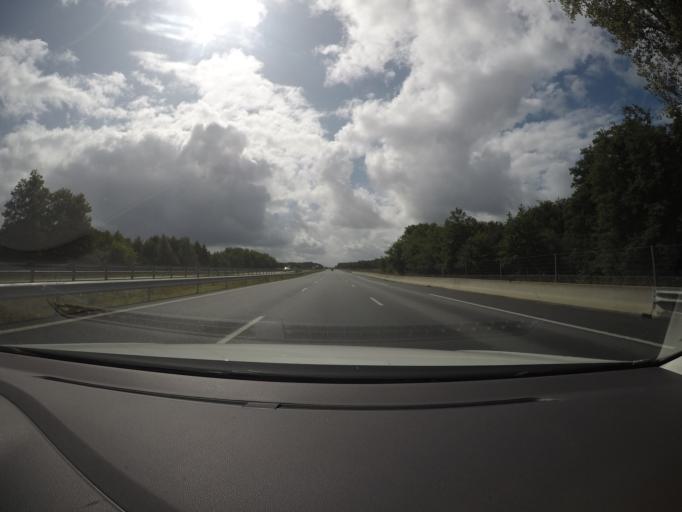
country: FR
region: Aquitaine
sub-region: Departement des Landes
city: Magescq
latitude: 43.7600
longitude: -1.2218
